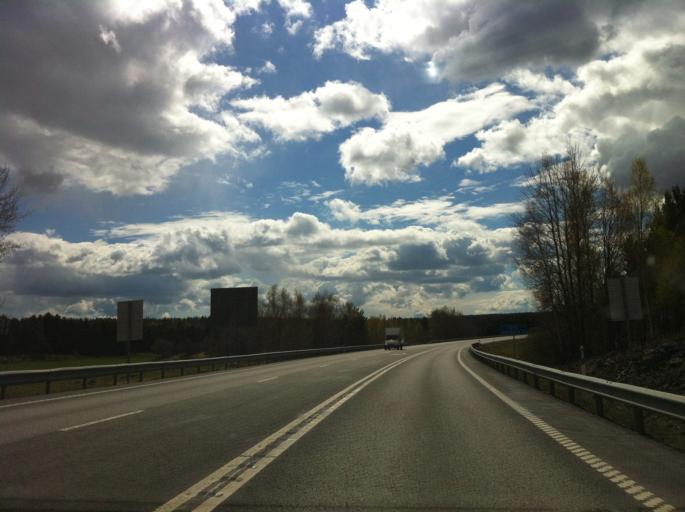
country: SE
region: Stockholm
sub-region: Osterakers Kommun
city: Akersberga
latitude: 59.5345
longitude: 18.1990
